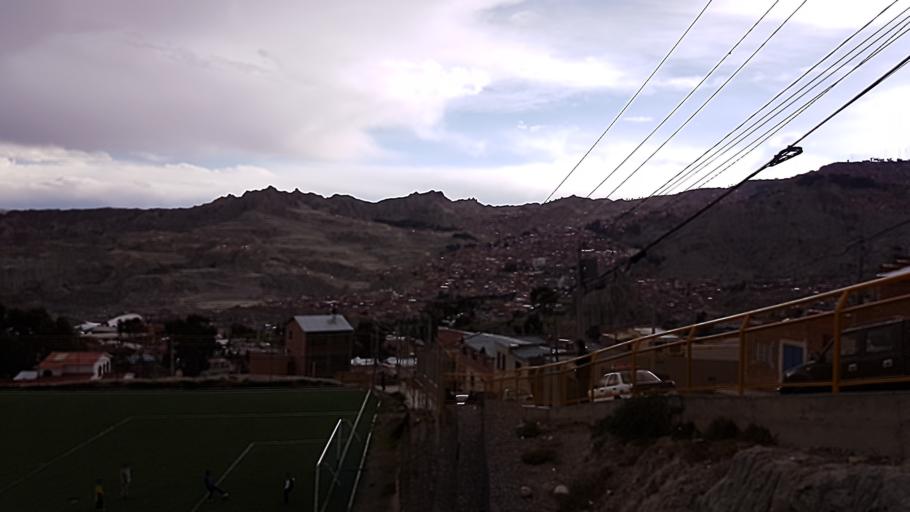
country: BO
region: La Paz
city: La Paz
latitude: -16.5121
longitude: -68.1109
